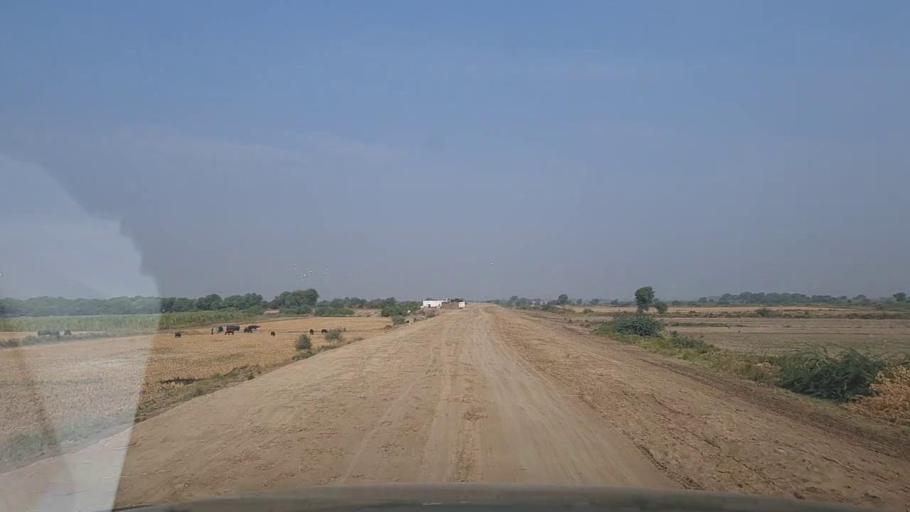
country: PK
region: Sindh
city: Bulri
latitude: 25.0010
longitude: 68.2889
